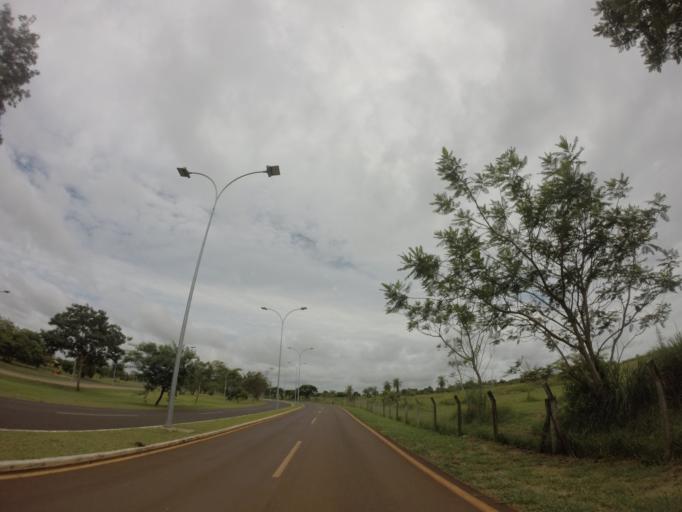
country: PY
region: Alto Parana
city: Ciudad del Este
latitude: -25.3893
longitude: -54.6303
